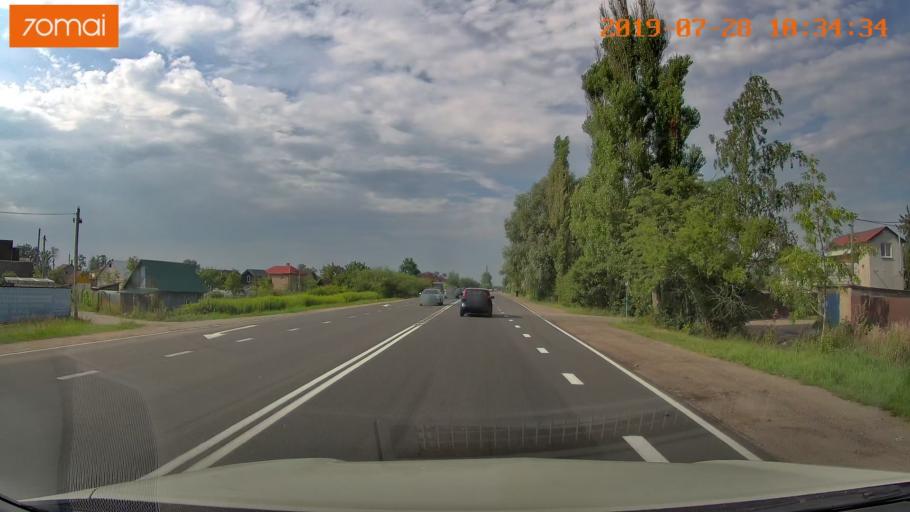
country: RU
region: Kaliningrad
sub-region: Gorod Kaliningrad
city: Kaliningrad
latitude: 54.7525
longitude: 20.4382
